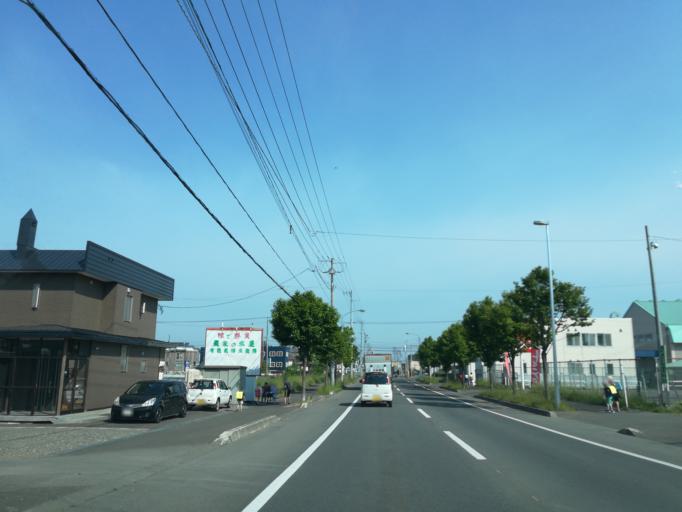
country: JP
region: Hokkaido
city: Iwamizawa
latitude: 43.2089
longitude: 141.7757
